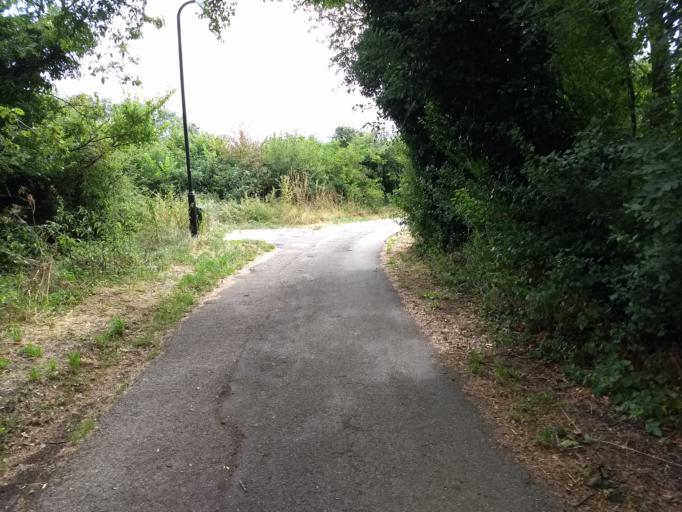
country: GB
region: England
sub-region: Milton Keynes
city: Newport Pagnell
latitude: 52.0754
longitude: -0.7251
